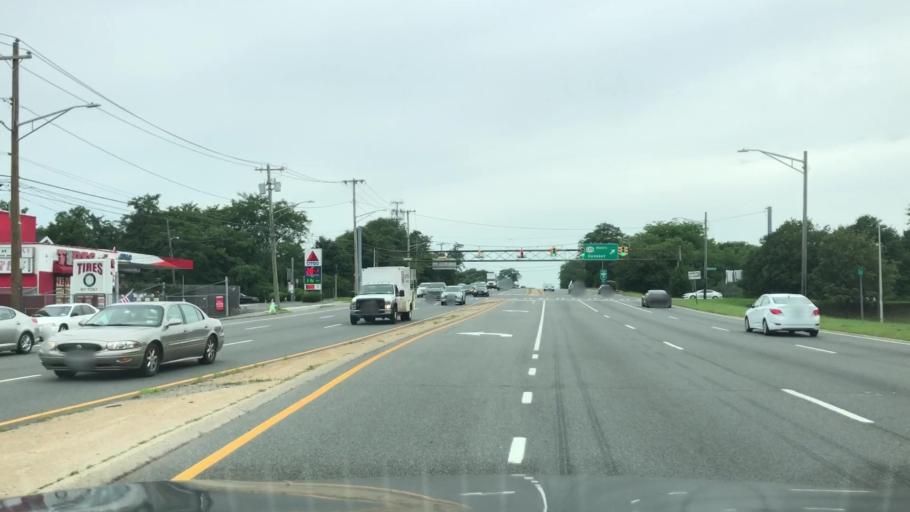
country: US
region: New York
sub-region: Nassau County
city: Seaford
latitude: 40.6746
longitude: -73.4903
